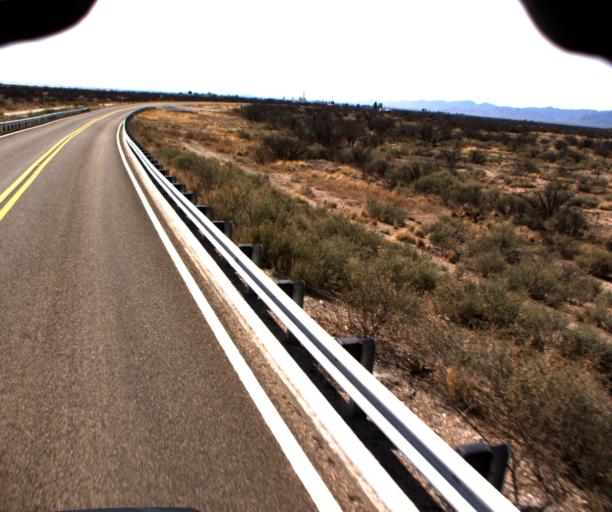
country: US
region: Arizona
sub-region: Cochise County
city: Willcox
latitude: 32.1321
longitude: -109.9097
